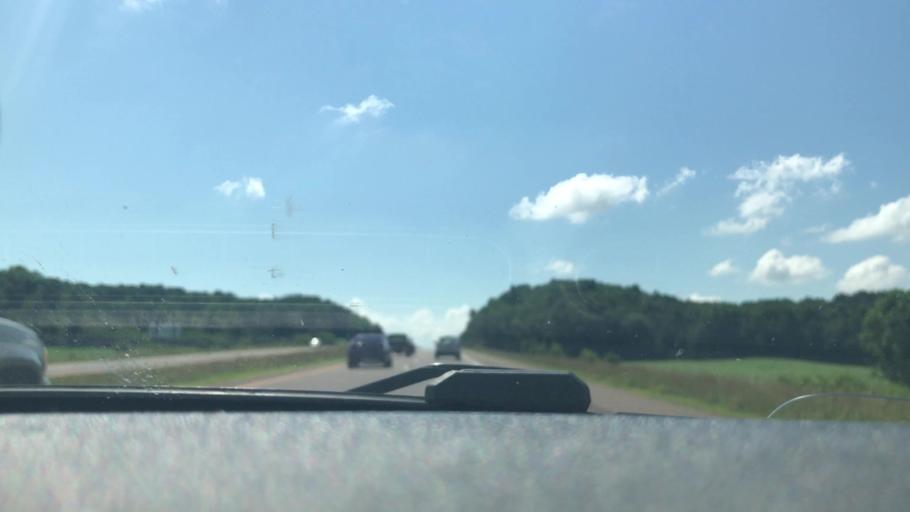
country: US
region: Wisconsin
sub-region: Chippewa County
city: Chippewa Falls
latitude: 44.9802
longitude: -91.4386
